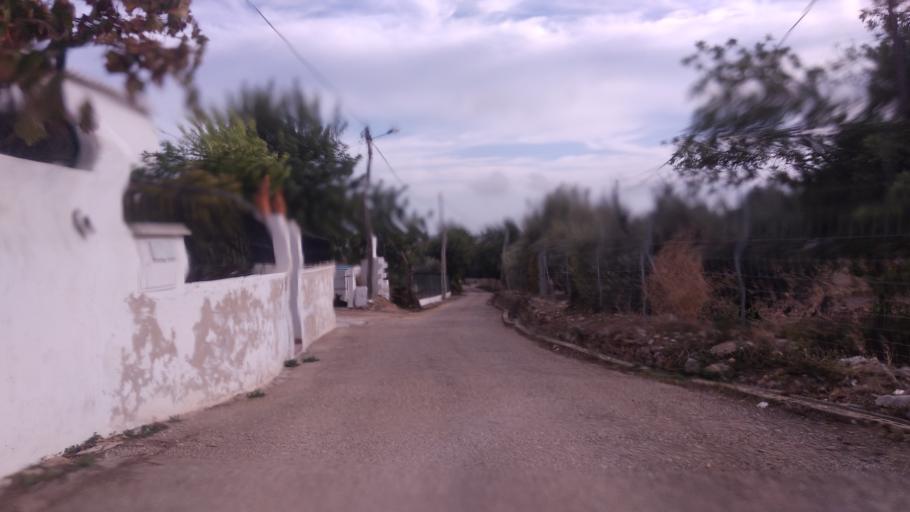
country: PT
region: Faro
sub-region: Sao Bras de Alportel
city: Sao Bras de Alportel
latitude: 37.1567
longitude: -7.8984
